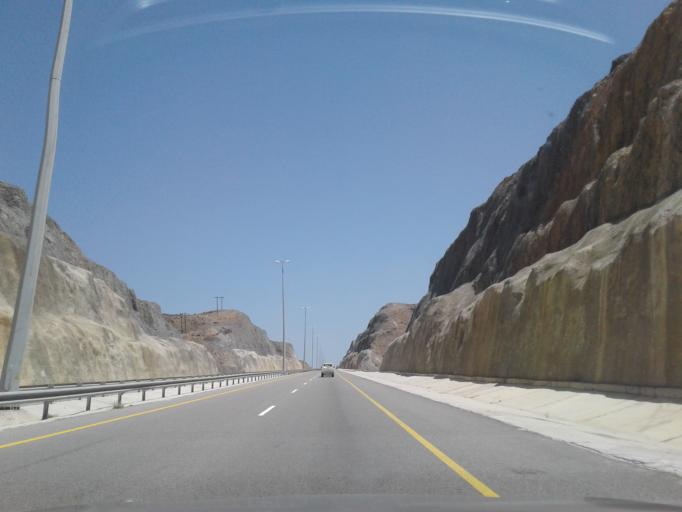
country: OM
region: Muhafazat Masqat
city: Muscat
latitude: 23.2113
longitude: 58.8026
